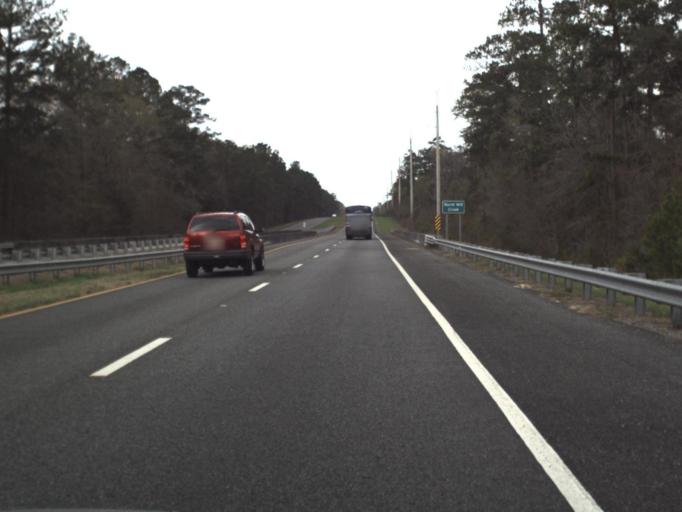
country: US
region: Florida
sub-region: Leon County
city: Woodville
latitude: 30.4076
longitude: -84.0633
